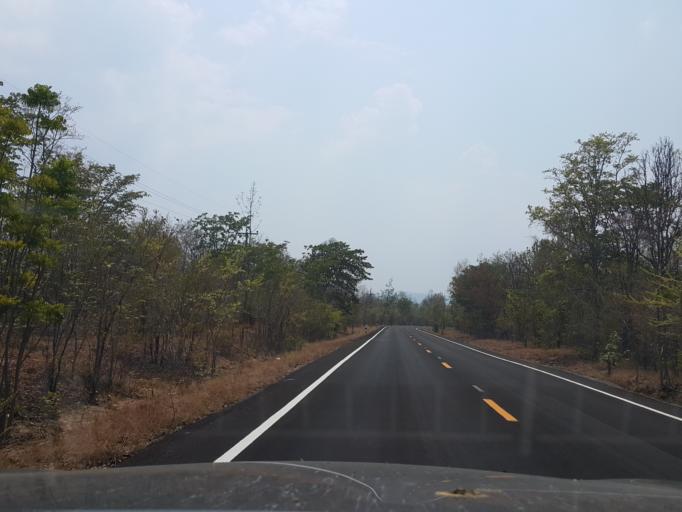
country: TH
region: Lampang
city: Mae Phrik
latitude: 17.4799
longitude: 99.1146
